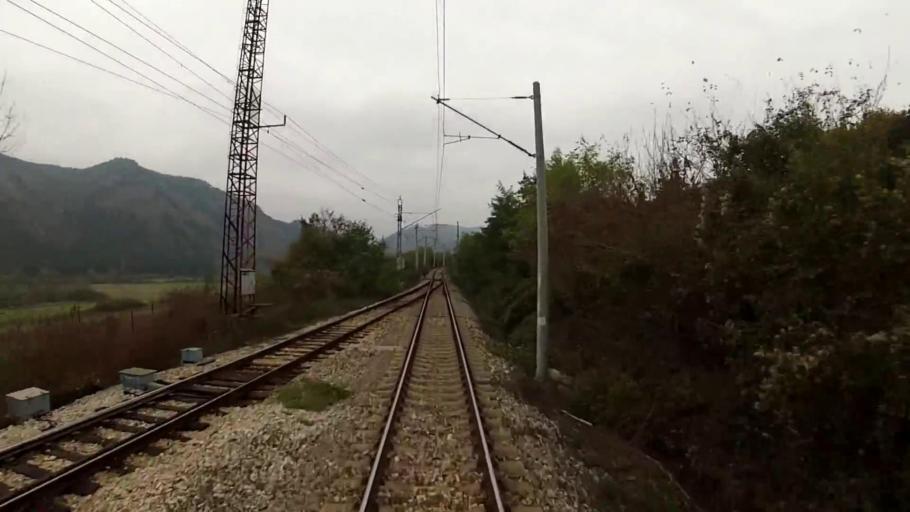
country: RS
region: Central Serbia
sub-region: Pirotski Okrug
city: Dimitrovgrad
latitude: 42.9891
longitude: 22.8516
